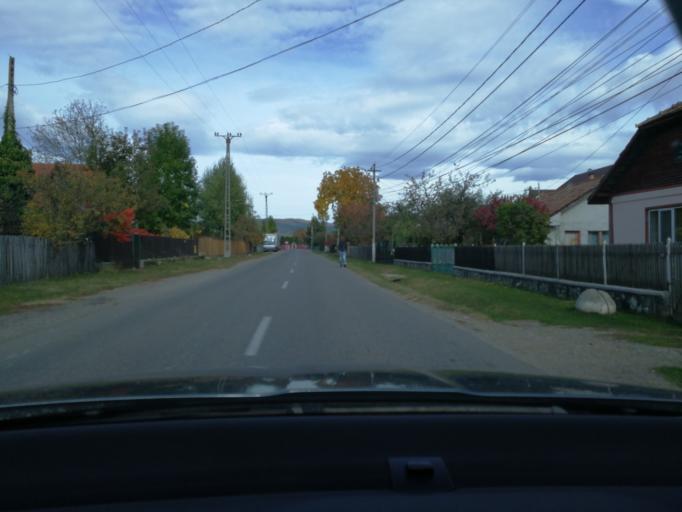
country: RO
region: Prahova
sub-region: Comuna Brebu
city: Brebu Megiesesc
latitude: 45.1578
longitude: 25.7744
